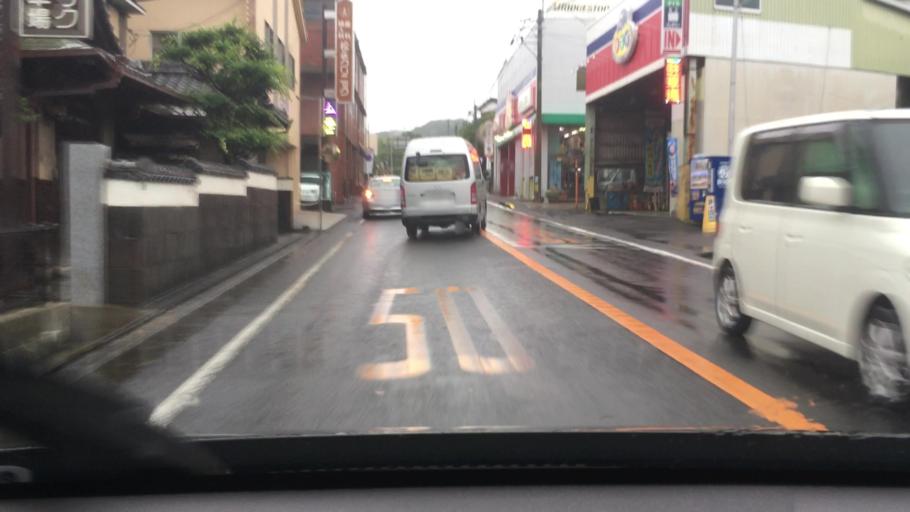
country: JP
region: Nagasaki
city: Sasebo
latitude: 33.1388
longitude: 129.7950
